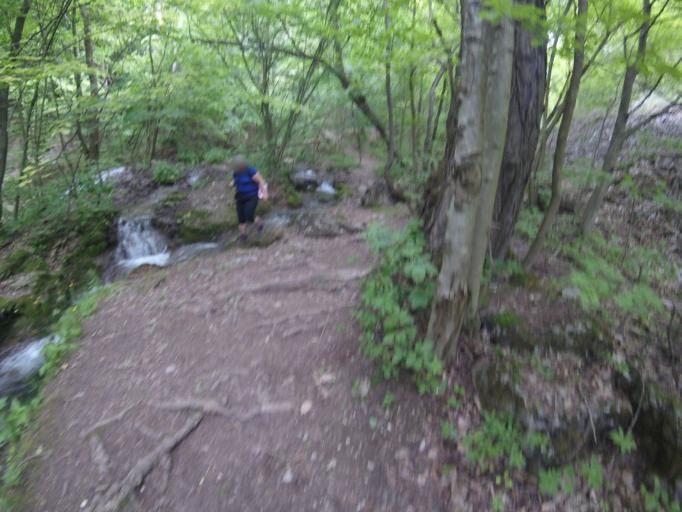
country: SK
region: Kosicky
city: Medzev
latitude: 48.6408
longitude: 20.8484
